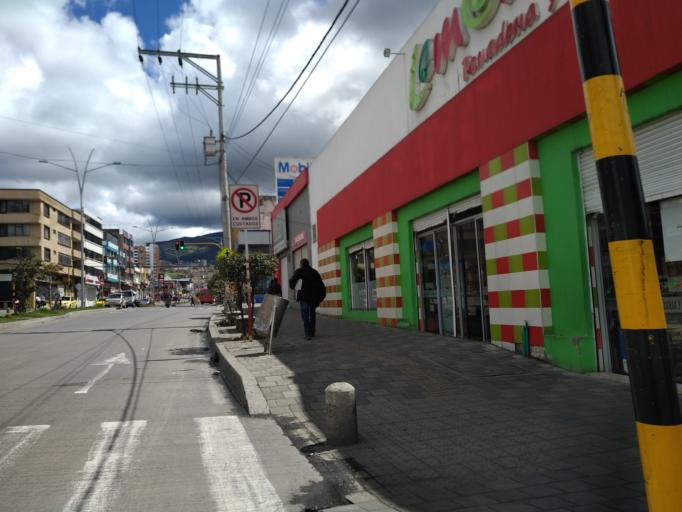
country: CO
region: Narino
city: Pasto
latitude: 1.2084
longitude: -77.2764
